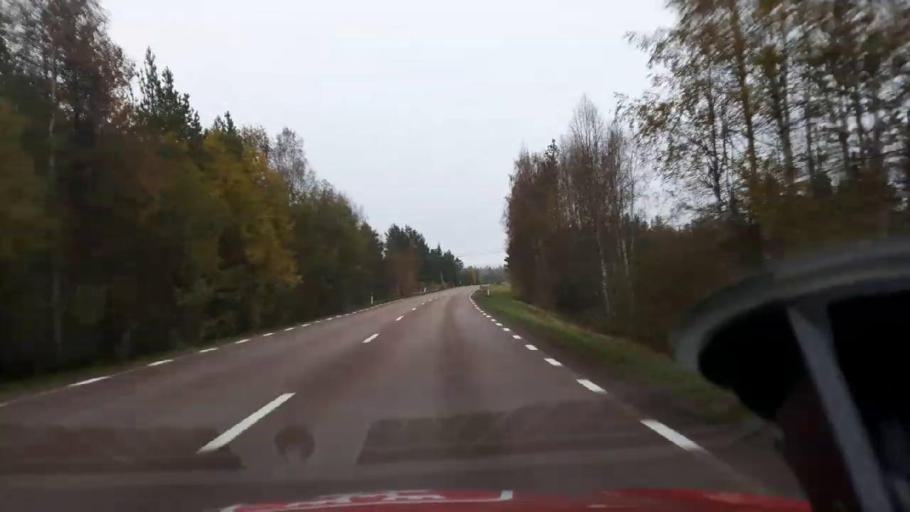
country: SE
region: Jaemtland
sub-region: Bergs Kommun
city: Hoverberg
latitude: 62.5161
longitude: 14.4495
